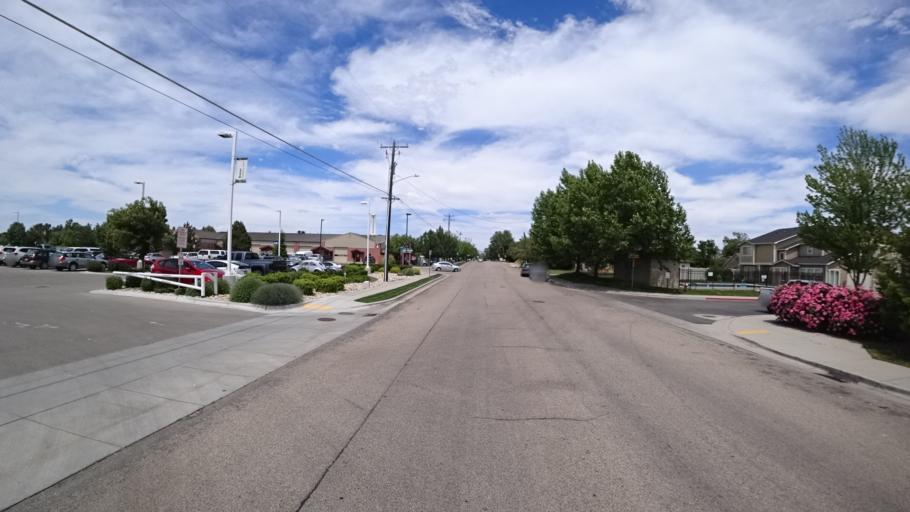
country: US
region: Idaho
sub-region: Ada County
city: Meridian
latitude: 43.6207
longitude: -116.3204
